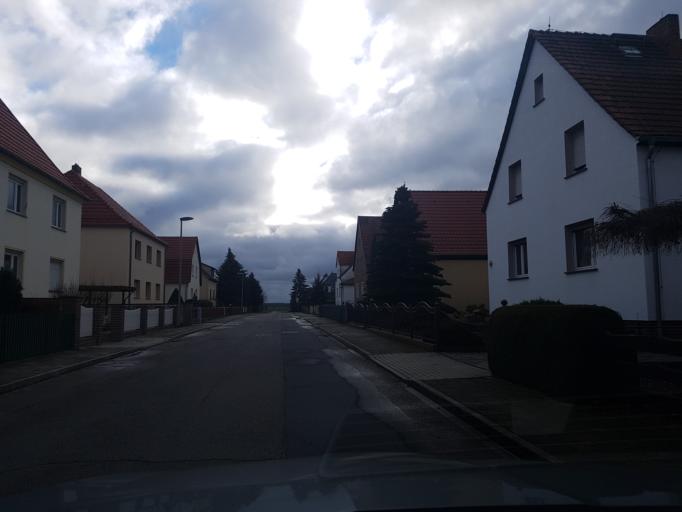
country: DE
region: Brandenburg
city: Herzberg
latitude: 51.6853
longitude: 13.2297
